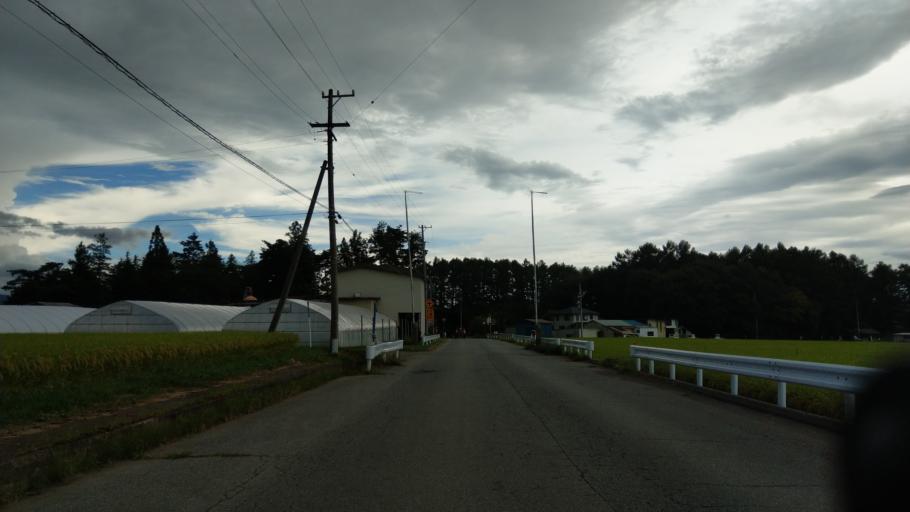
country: JP
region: Nagano
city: Komoro
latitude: 36.3024
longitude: 138.4774
